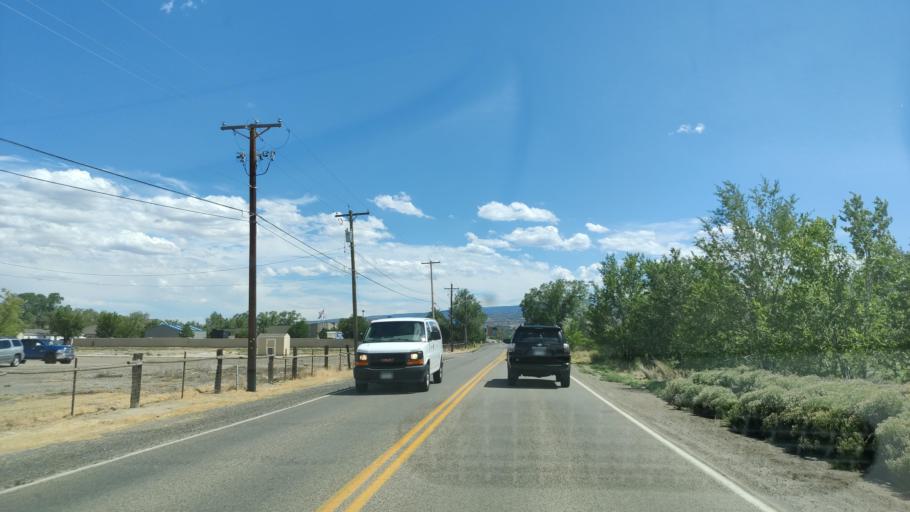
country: US
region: Colorado
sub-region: Mesa County
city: Redlands
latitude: 39.0986
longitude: -108.5988
